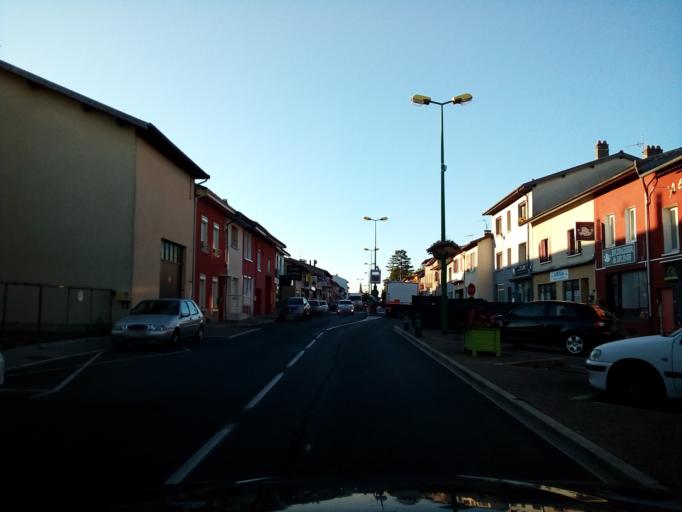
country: FR
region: Rhone-Alpes
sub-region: Departement de l'Isere
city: La Verpilliere
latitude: 45.6385
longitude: 5.1412
